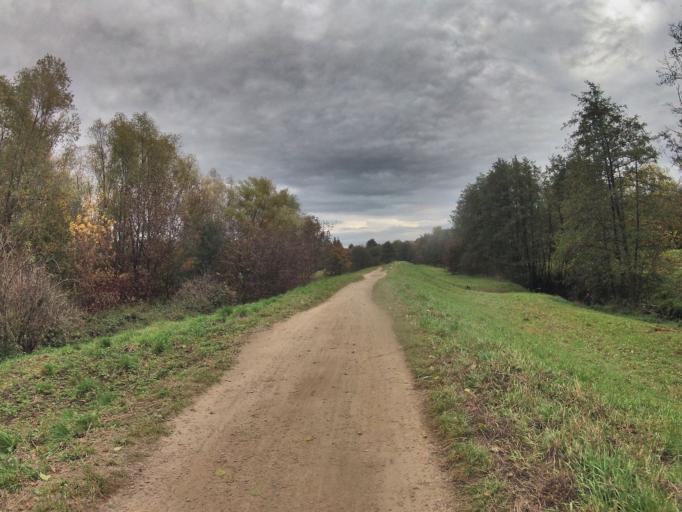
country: PL
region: Lesser Poland Voivodeship
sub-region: Krakow
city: Krakow
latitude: 50.0657
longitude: 19.8920
